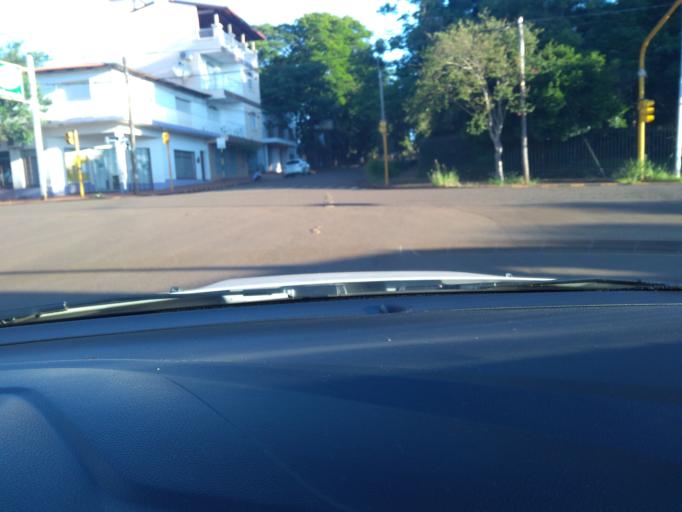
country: AR
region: Misiones
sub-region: Departamento de Obera
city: Obera
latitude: -27.4820
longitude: -55.1127
